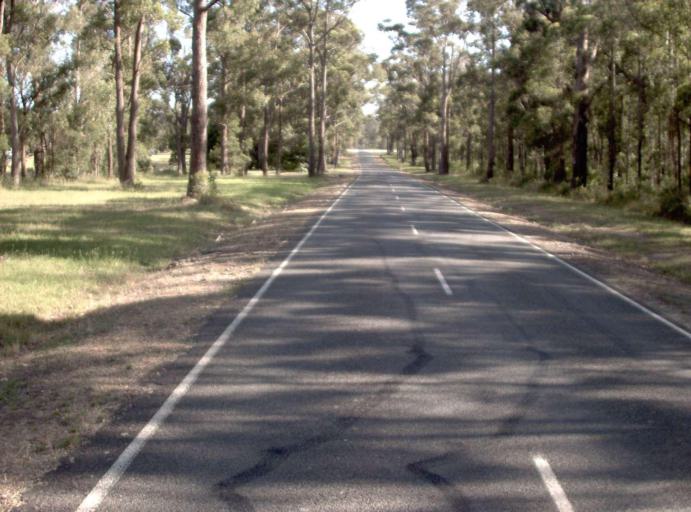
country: AU
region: Victoria
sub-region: East Gippsland
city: Lakes Entrance
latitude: -37.6816
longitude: 148.4706
